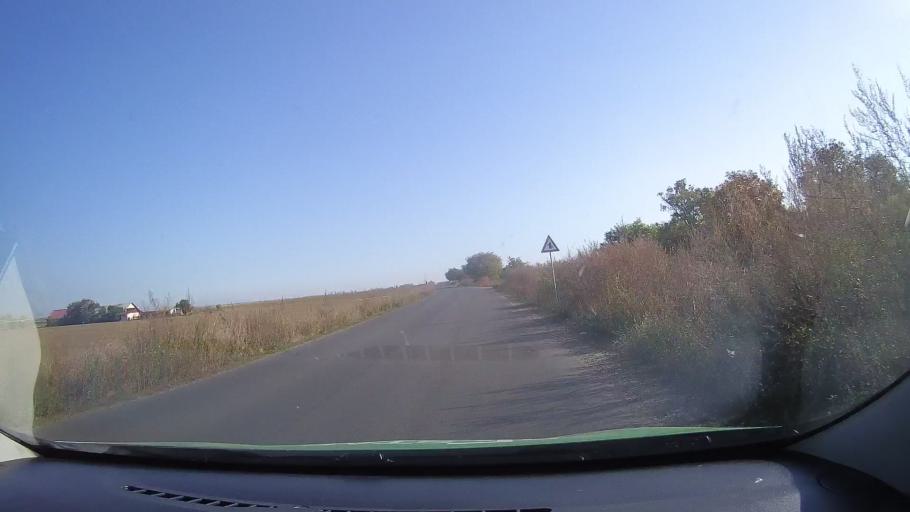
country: RO
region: Satu Mare
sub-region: Comuna Sauca
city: Sauca
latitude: 47.4944
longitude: 22.4792
